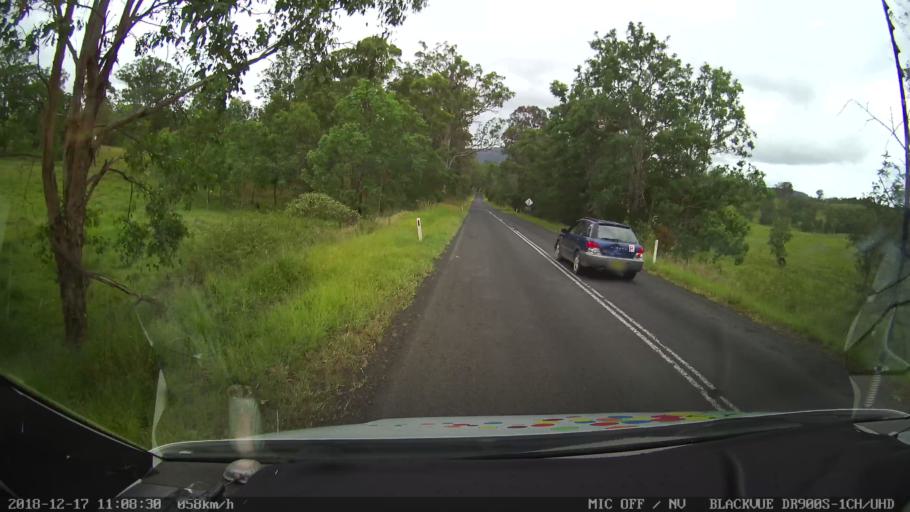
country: AU
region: New South Wales
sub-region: Kyogle
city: Kyogle
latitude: -28.7630
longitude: 152.6546
